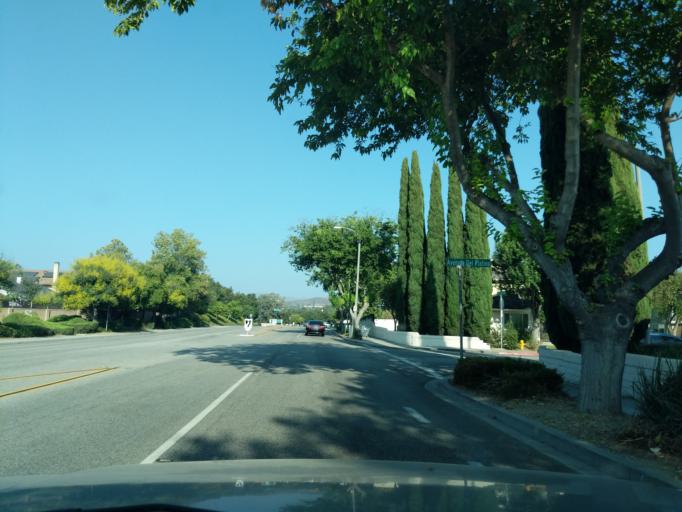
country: US
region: California
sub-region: Ventura County
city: Casa Conejo
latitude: 34.1883
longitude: -118.9137
